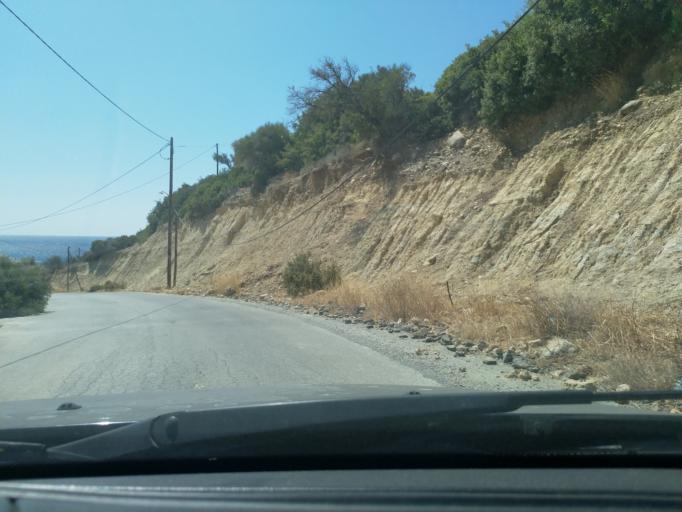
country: GR
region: Crete
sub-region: Nomos Rethymnis
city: Agia Galini
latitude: 35.1199
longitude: 24.5488
